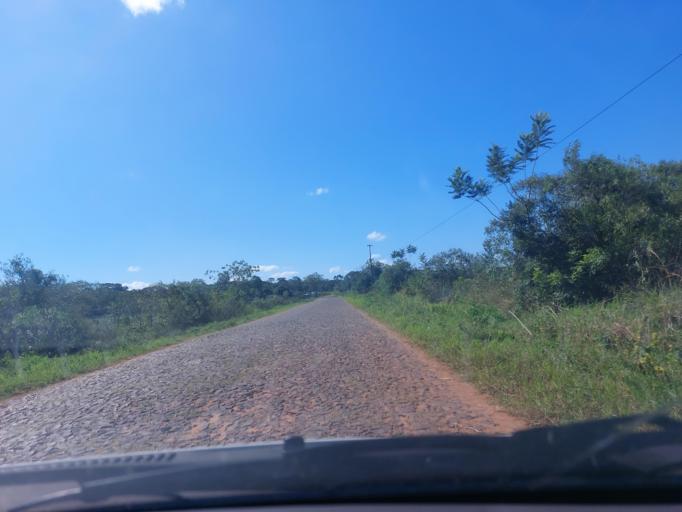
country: PY
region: San Pedro
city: Itacurubi del Rosario
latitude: -24.5863
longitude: -56.6010
